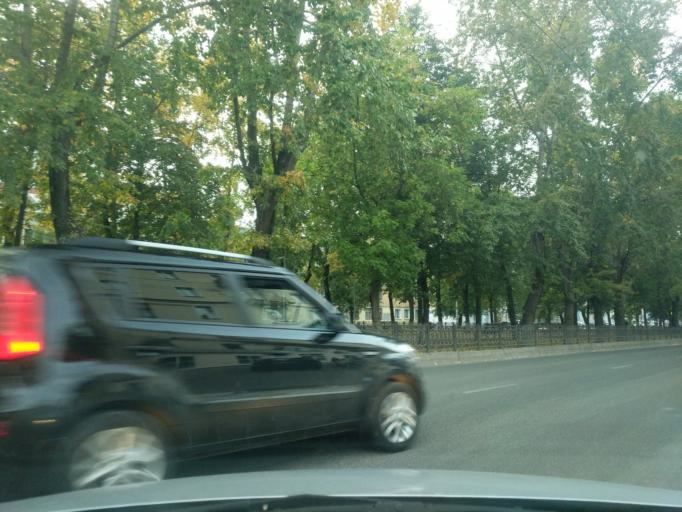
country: RU
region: Kirov
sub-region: Kirovo-Chepetskiy Rayon
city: Kirov
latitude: 58.6102
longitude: 49.6574
